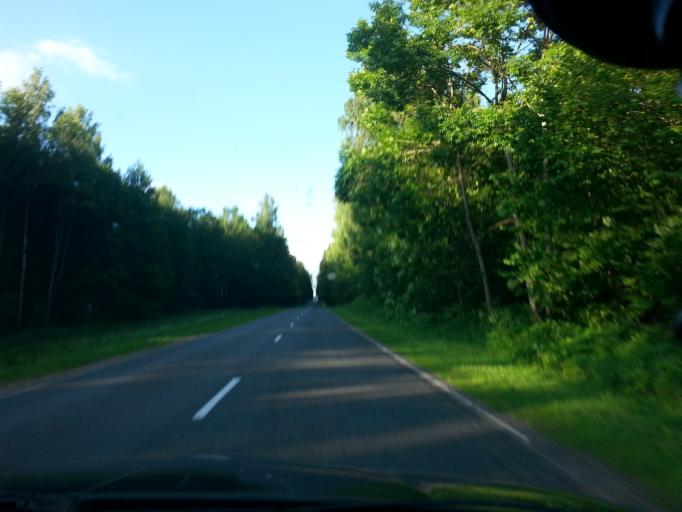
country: BY
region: Minsk
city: Svir
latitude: 54.9048
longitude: 26.4238
